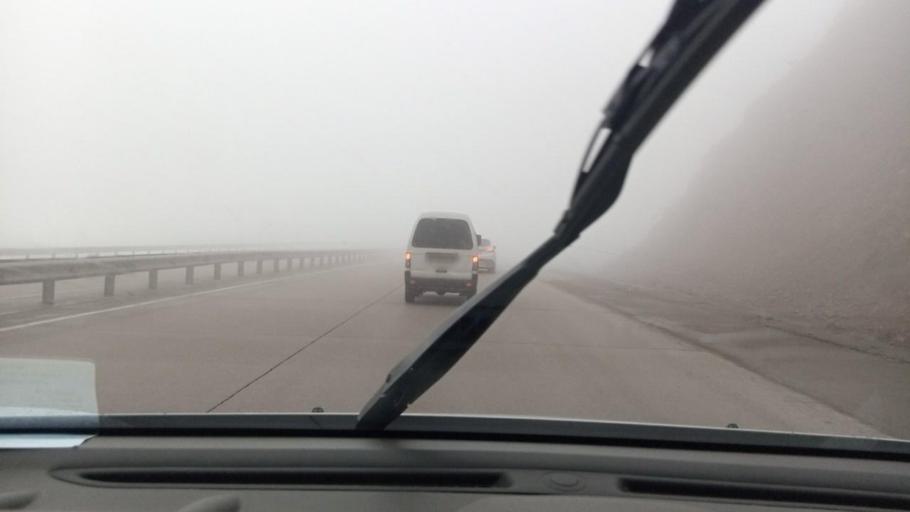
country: UZ
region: Toshkent
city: Angren
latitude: 41.1049
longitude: 70.5119
